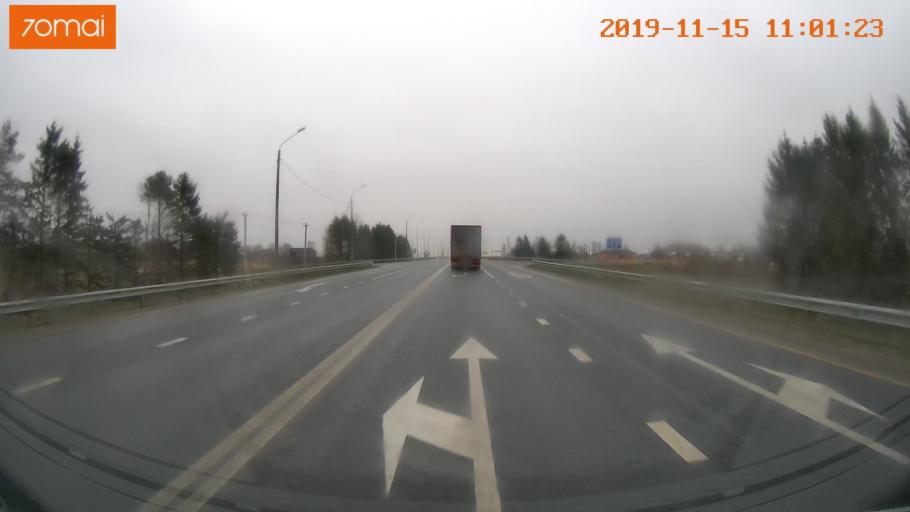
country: RU
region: Vologda
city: Chebsara
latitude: 59.1331
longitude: 38.9196
